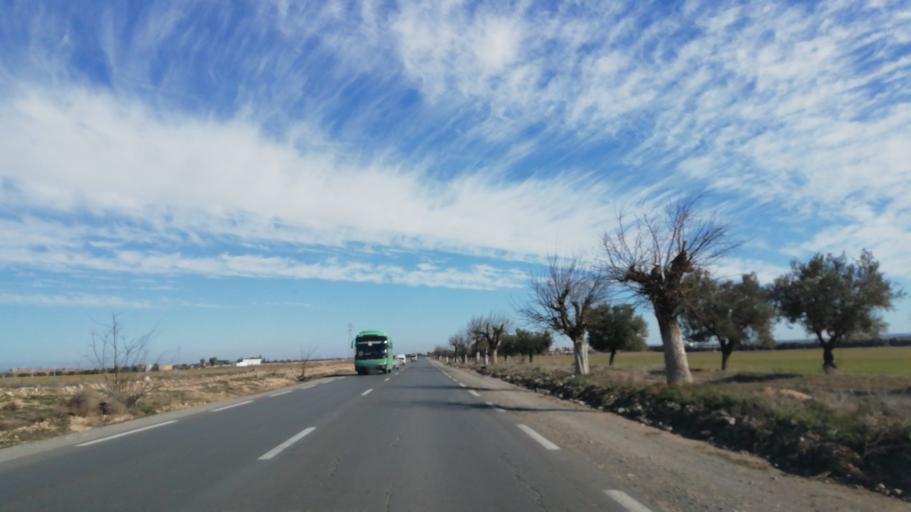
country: DZ
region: Sidi Bel Abbes
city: Sidi Bel Abbes
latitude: 35.1070
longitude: -0.7434
